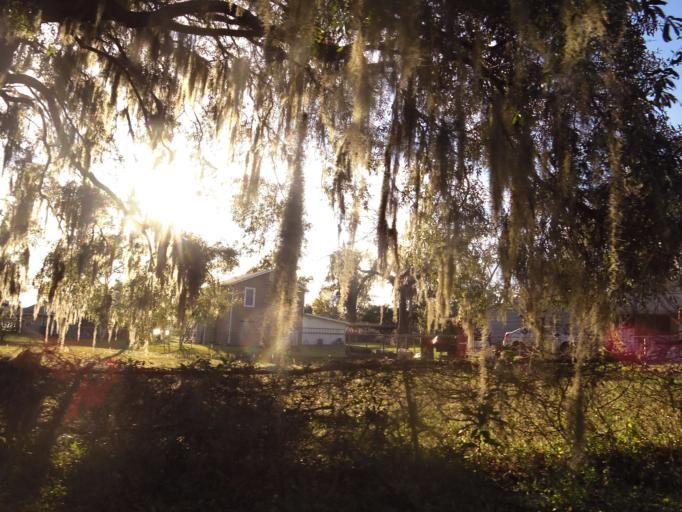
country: US
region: Florida
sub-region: Duval County
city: Jacksonville
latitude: 30.4371
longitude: -81.6128
